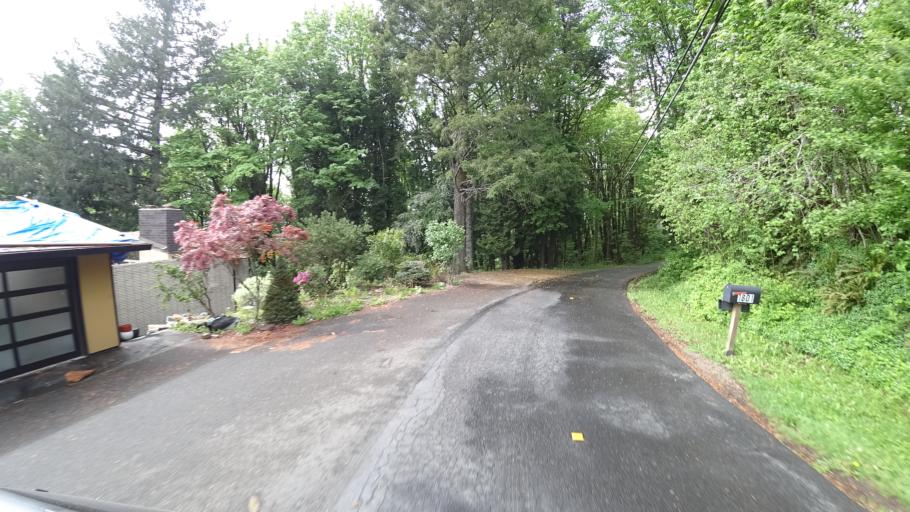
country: US
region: Oregon
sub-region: Washington County
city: West Haven
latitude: 45.5351
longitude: -122.7568
